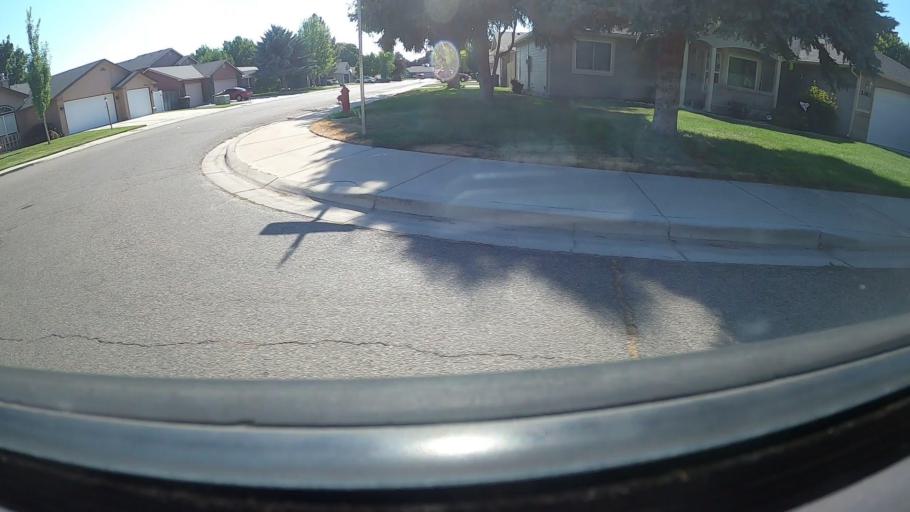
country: US
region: Idaho
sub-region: Ada County
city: Meridian
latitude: 43.6264
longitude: -116.3659
